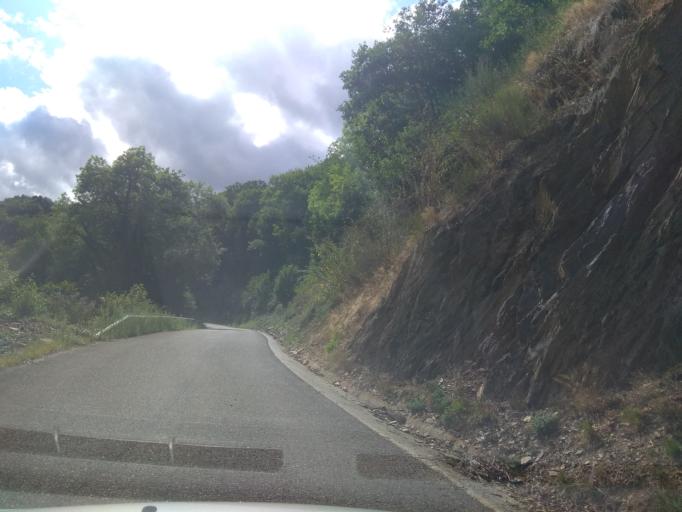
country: ES
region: Catalonia
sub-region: Provincia de Lleida
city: Les
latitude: 42.8312
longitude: 0.7259
